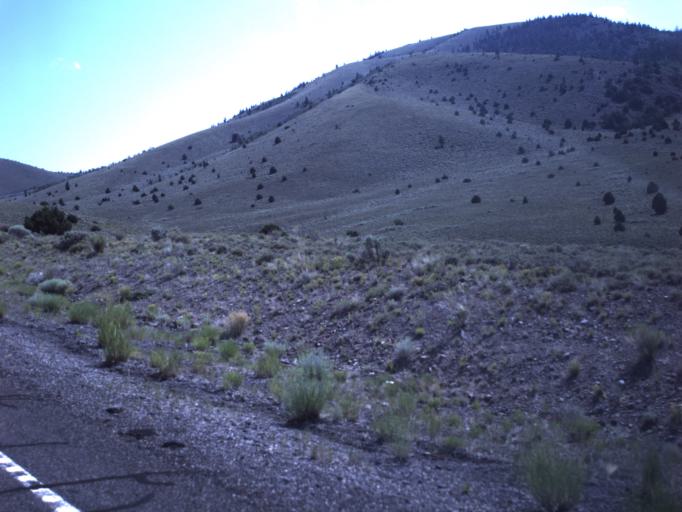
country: US
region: Utah
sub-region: Wayne County
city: Loa
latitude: 38.5368
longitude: -111.5142
